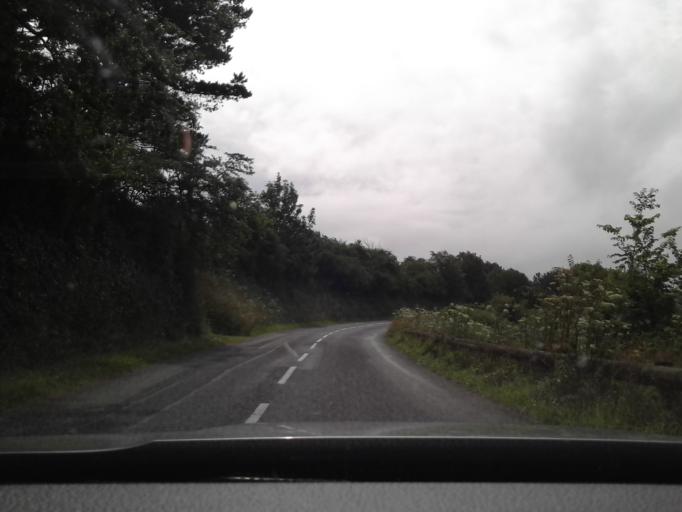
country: FR
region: Lower Normandy
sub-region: Departement de la Manche
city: Urville-Nacqueville
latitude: 49.6792
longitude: -1.7706
